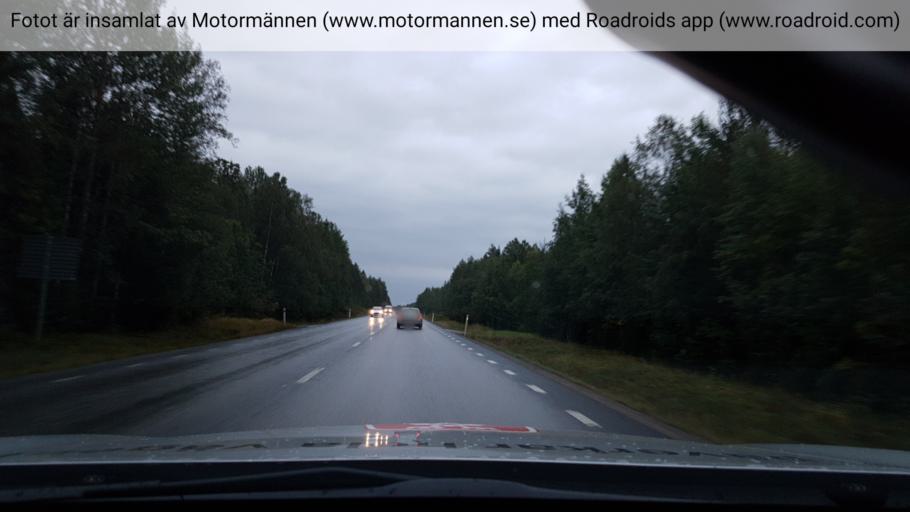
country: SE
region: Vaesterbotten
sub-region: Umea Kommun
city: Roback
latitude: 63.8499
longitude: 20.1111
